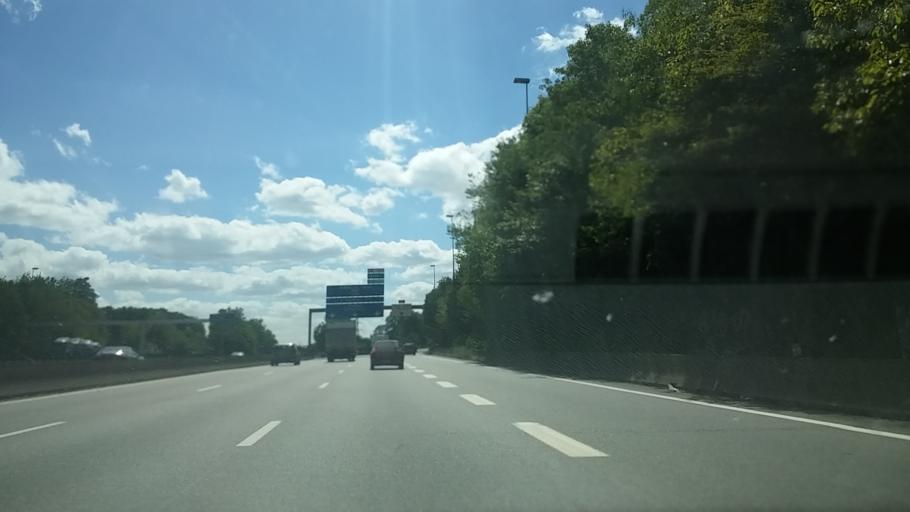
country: FR
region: Ile-de-France
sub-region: Departement des Yvelines
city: Fontenay-le-Fleury
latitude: 48.8020
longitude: 2.0468
